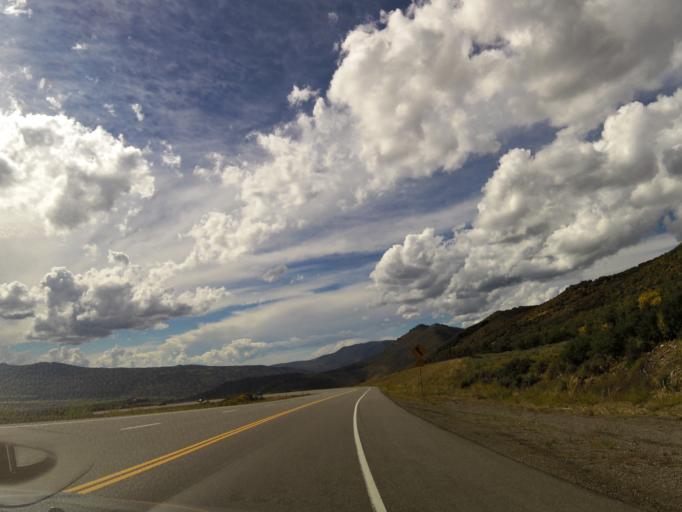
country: US
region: Colorado
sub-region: Hinsdale County
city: Lake City
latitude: 38.3961
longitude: -107.4500
